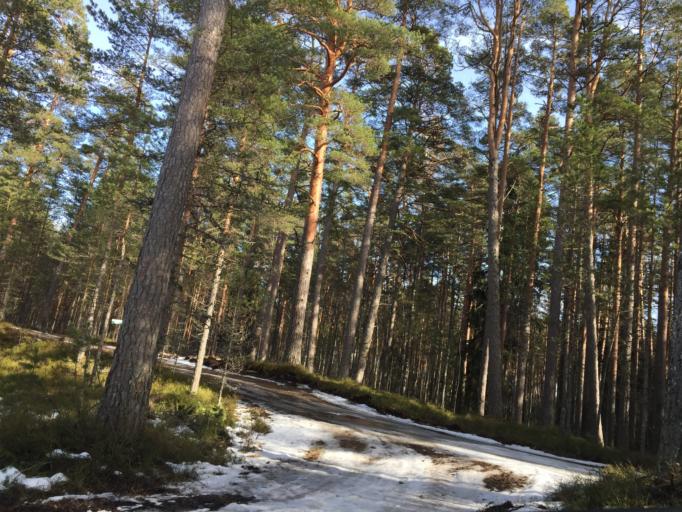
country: EE
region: Paernumaa
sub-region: Paernu linn
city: Parnu
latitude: 58.2305
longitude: 24.5190
